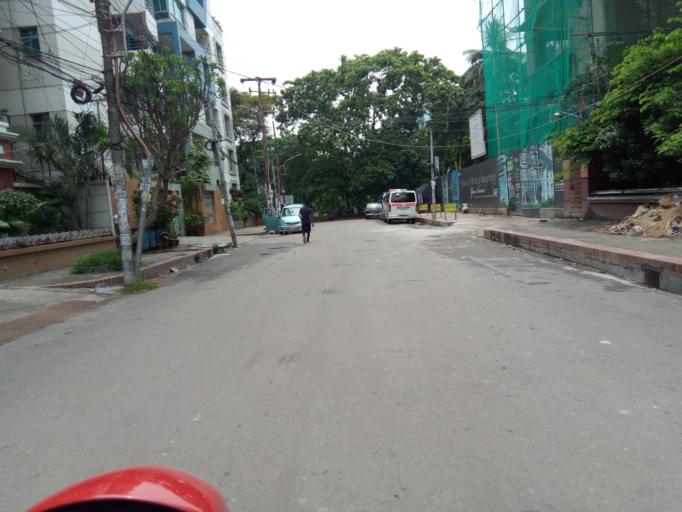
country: BD
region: Dhaka
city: Azimpur
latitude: 23.7397
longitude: 90.3782
